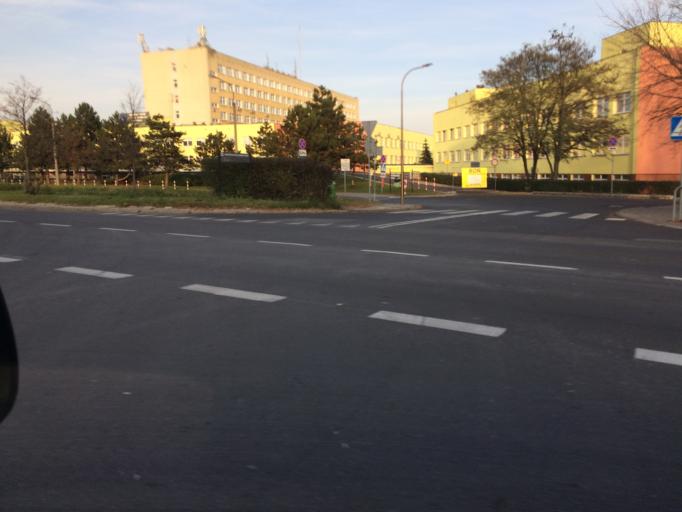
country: PL
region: Opole Voivodeship
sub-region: Powiat opolski
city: Opole
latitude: 50.6754
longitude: 17.9749
